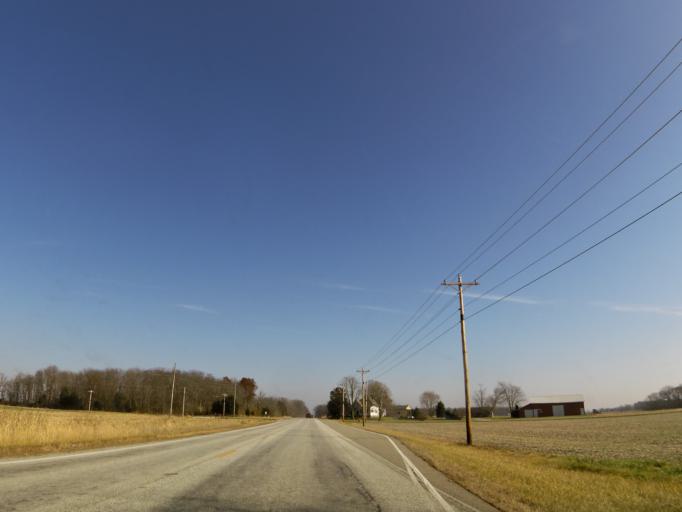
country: US
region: Indiana
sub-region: Shelby County
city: Shelbyville
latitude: 39.5433
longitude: -85.6963
